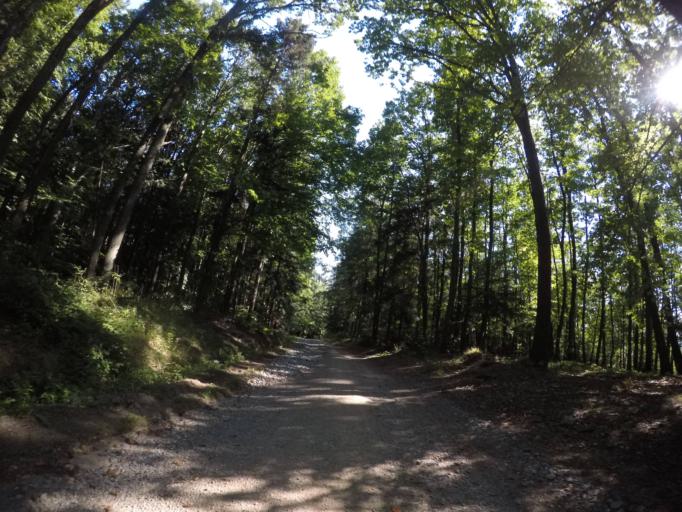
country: SK
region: Kosicky
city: Kosice
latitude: 48.7424
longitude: 21.1931
